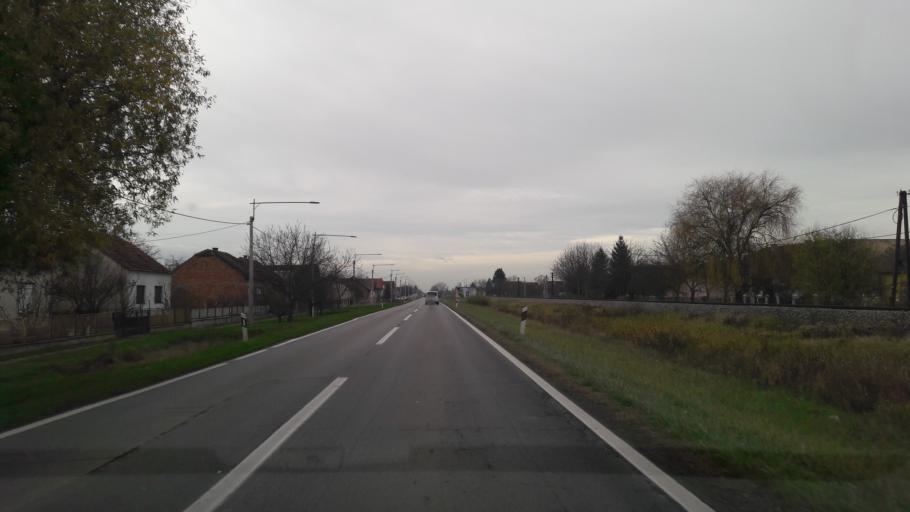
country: HR
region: Osjecko-Baranjska
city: Bizovac
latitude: 45.5717
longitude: 18.4042
